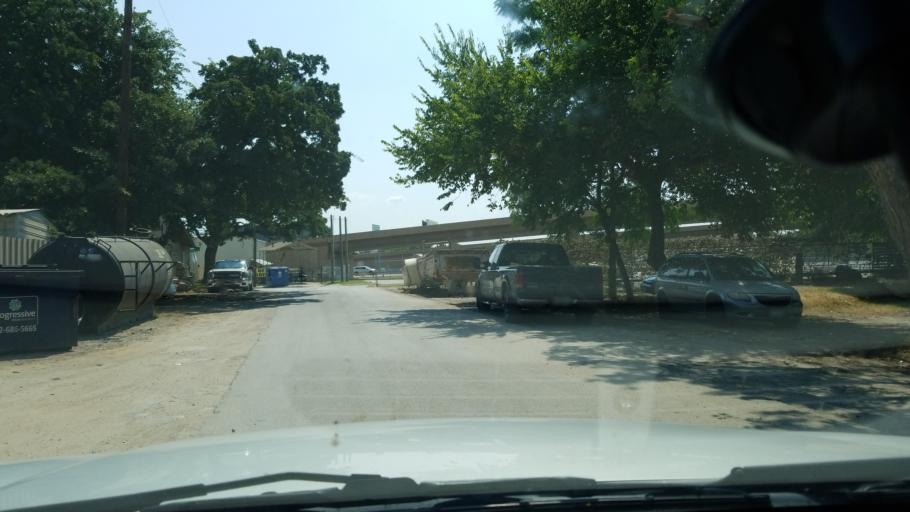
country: US
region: Texas
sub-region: Dallas County
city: Irving
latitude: 32.8603
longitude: -96.9037
